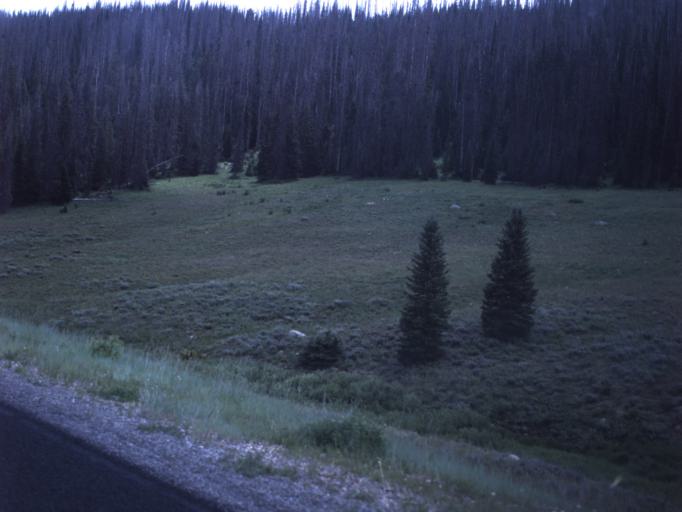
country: US
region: Utah
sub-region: Summit County
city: Francis
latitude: 40.4852
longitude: -111.0136
